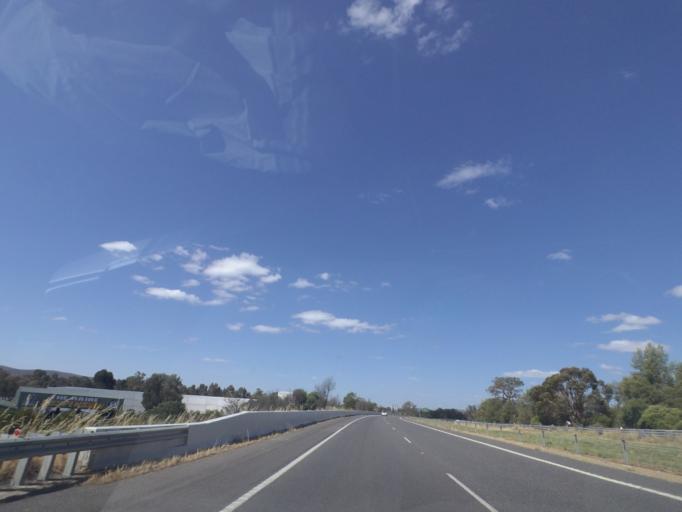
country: AU
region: Victoria
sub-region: Wodonga
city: Wodonga
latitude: -36.1080
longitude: 146.8626
